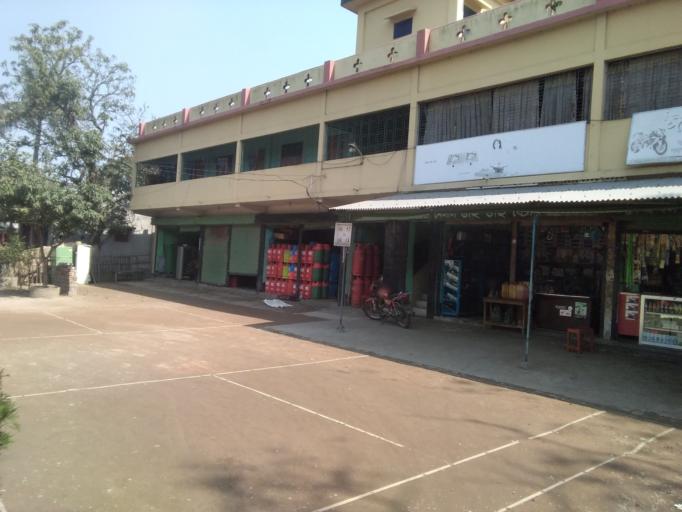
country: IN
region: West Bengal
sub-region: North 24 Parganas
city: Taki
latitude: 22.5921
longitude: 89.0008
